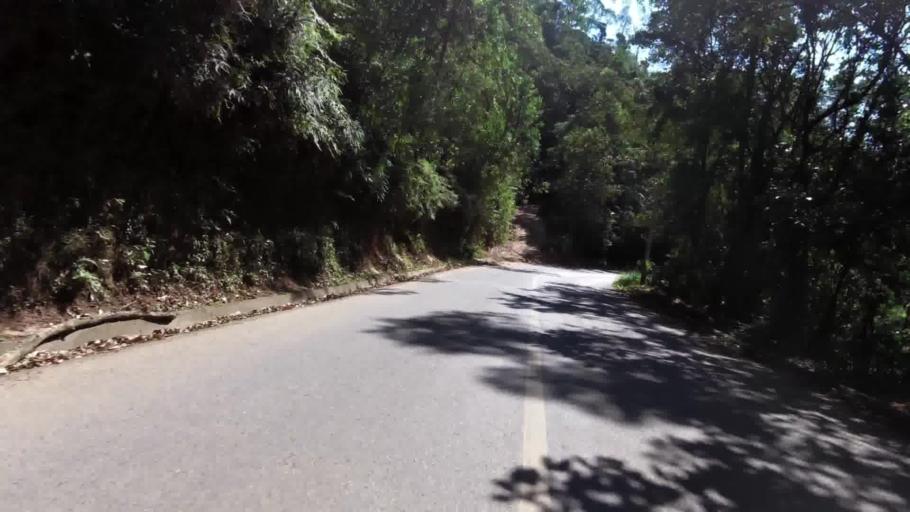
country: BR
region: Espirito Santo
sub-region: Marechal Floriano
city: Marechal Floriano
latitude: -20.4512
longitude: -40.8927
